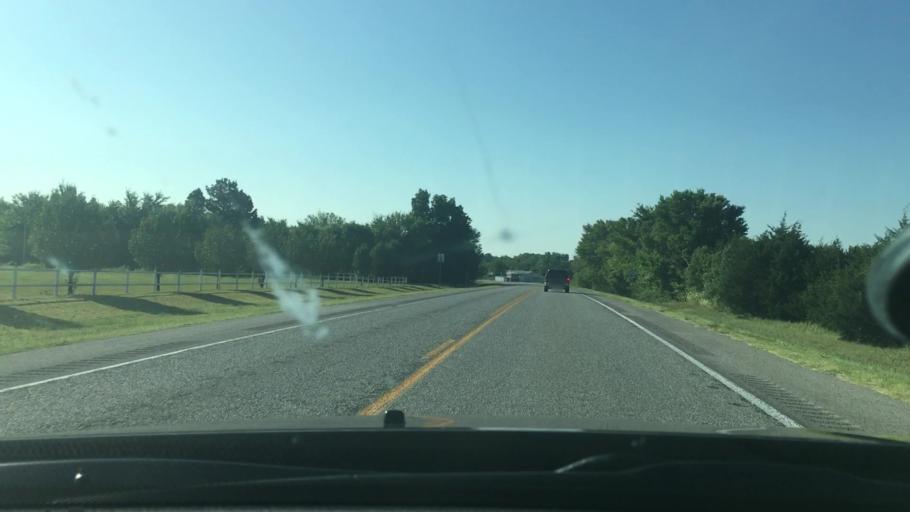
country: US
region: Oklahoma
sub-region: Johnston County
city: Tishomingo
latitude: 34.2502
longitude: -96.7596
